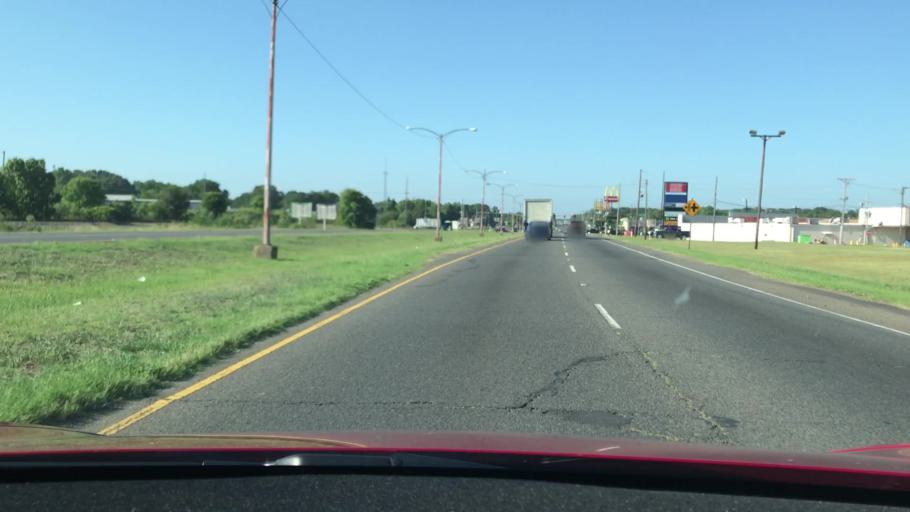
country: US
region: Louisiana
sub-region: Caddo Parish
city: Shreveport
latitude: 32.4447
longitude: -93.7804
